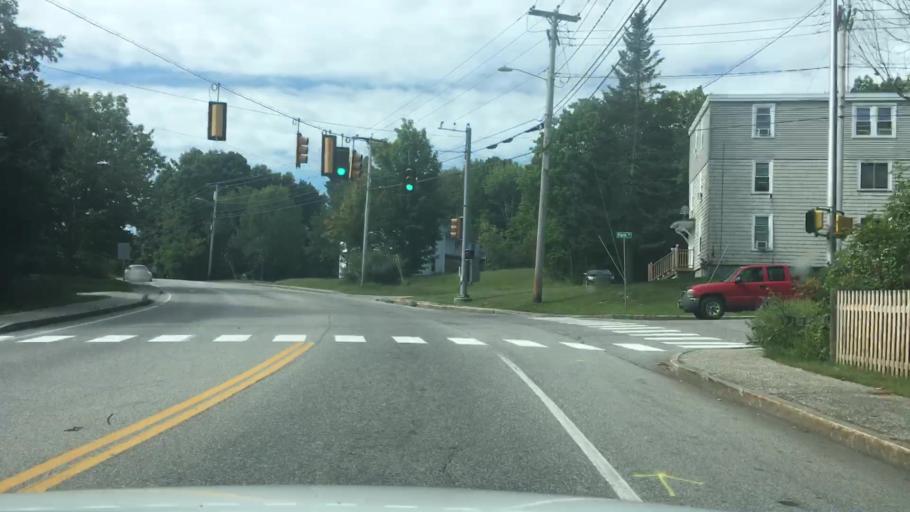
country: US
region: Maine
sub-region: Androscoggin County
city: Auburn
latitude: 44.0943
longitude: -70.2445
